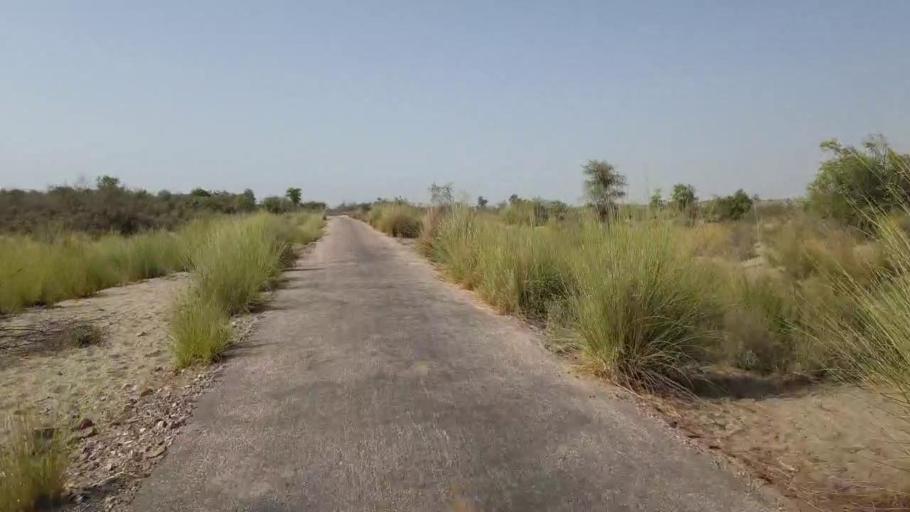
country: PK
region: Sindh
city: Jam Sahib
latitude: 26.5896
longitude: 68.9219
